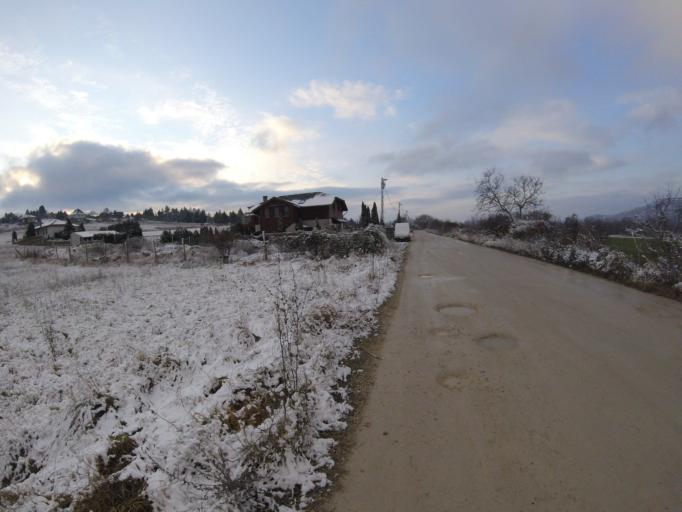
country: HU
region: Komarom-Esztergom
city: Esztergom
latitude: 47.8037
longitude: 18.7682
